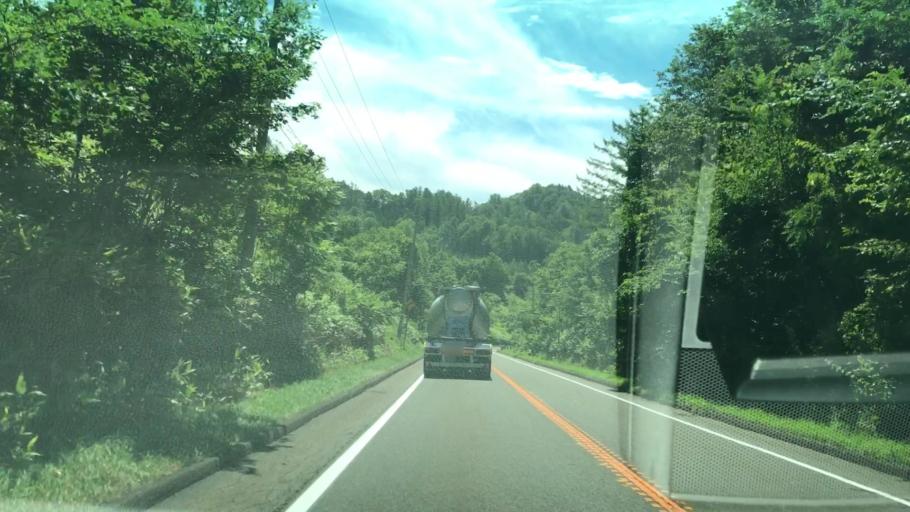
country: JP
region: Hokkaido
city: Shimo-furano
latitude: 42.9036
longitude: 142.4371
